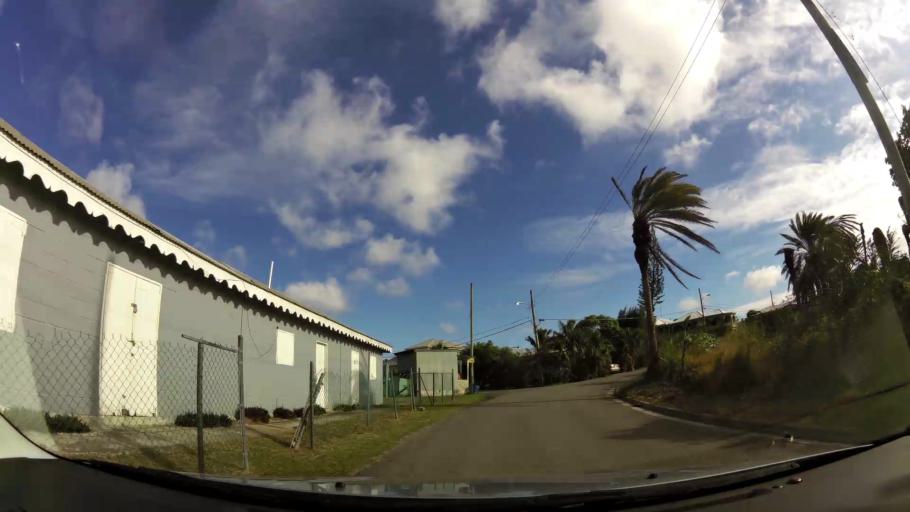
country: AG
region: Saint Peter
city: All Saints
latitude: 17.0690
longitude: -61.7909
